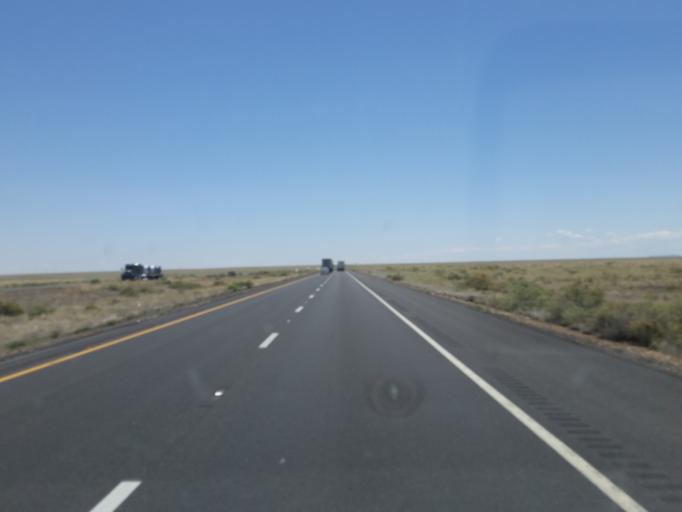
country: US
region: Arizona
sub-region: Coconino County
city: Flagstaff
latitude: 35.1451
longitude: -111.2278
